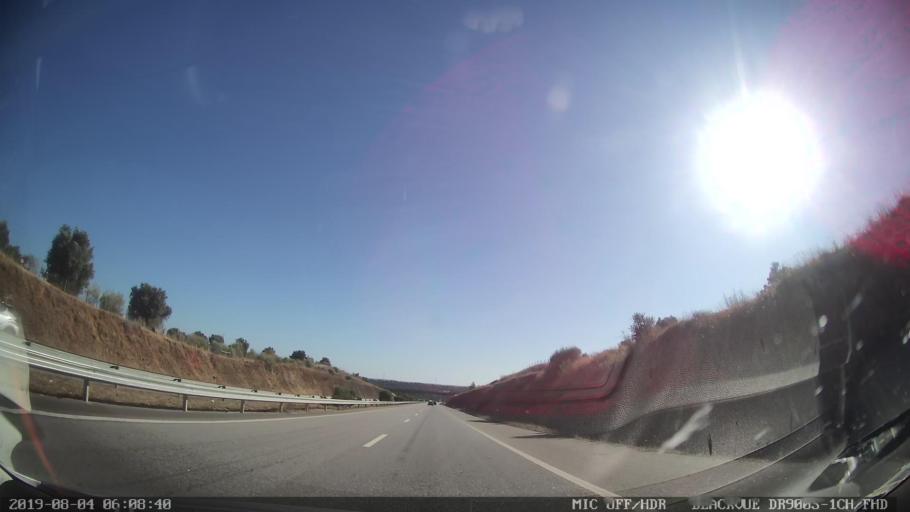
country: PT
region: Santarem
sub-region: Abrantes
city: Alferrarede
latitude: 39.4907
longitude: -8.1184
